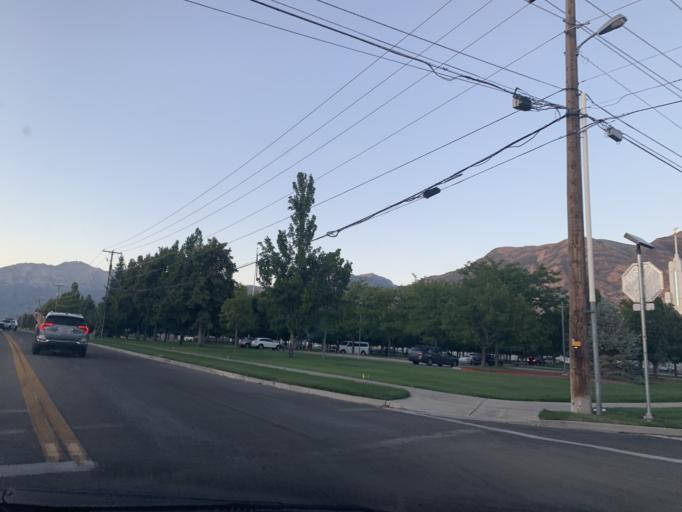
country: US
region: Utah
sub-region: Utah County
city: Cedar Hills
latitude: 40.3919
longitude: -111.7733
